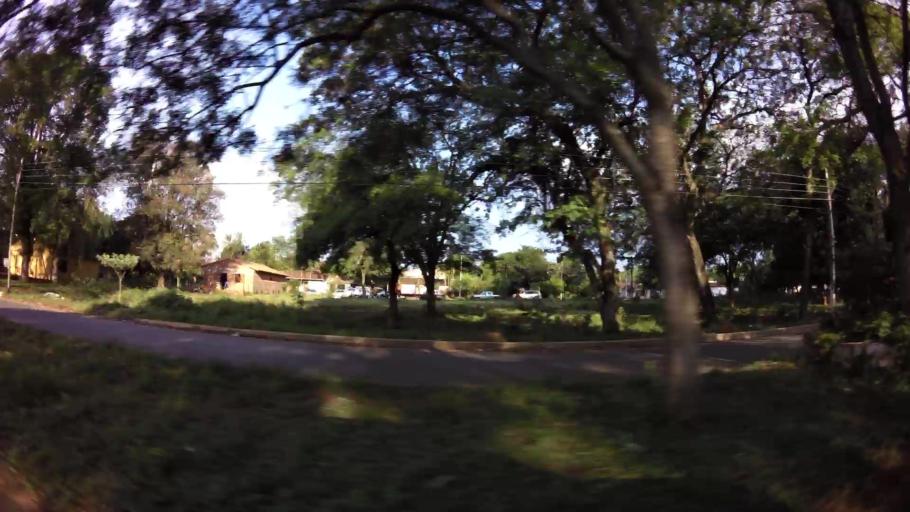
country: PY
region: Central
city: Fernando de la Mora
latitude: -25.3579
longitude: -57.5220
